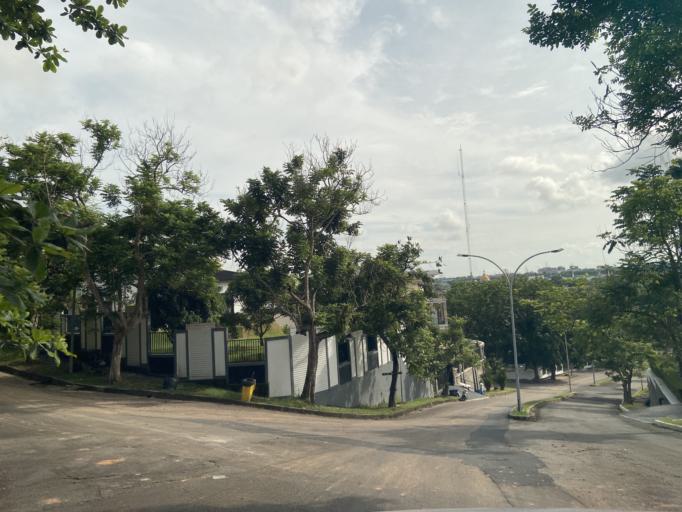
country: SG
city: Singapore
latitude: 1.1100
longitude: 104.0216
